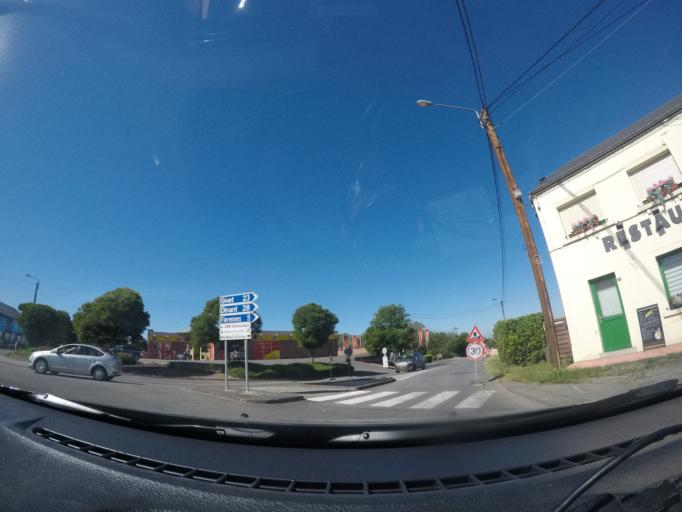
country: BE
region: Wallonia
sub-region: Province de Namur
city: Philippeville
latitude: 50.1966
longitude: 4.5362
